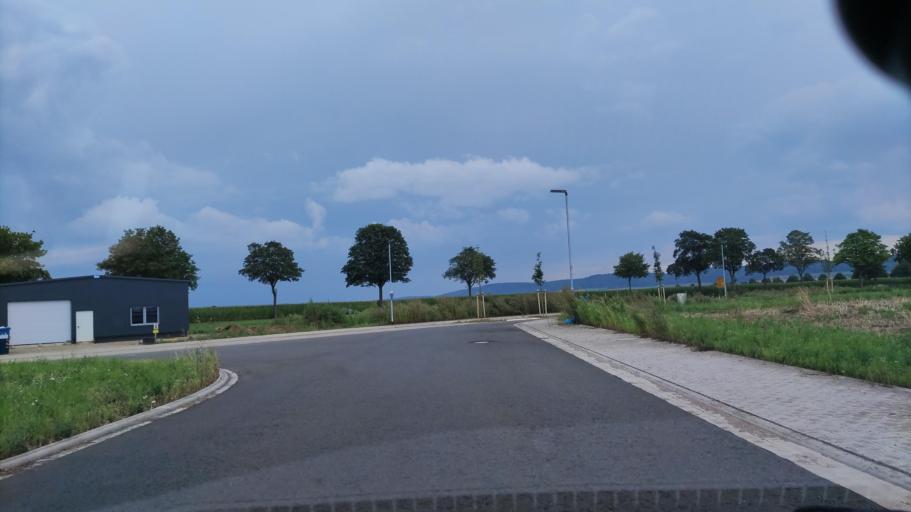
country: DE
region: Lower Saxony
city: Banteln
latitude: 52.0841
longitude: 9.7537
